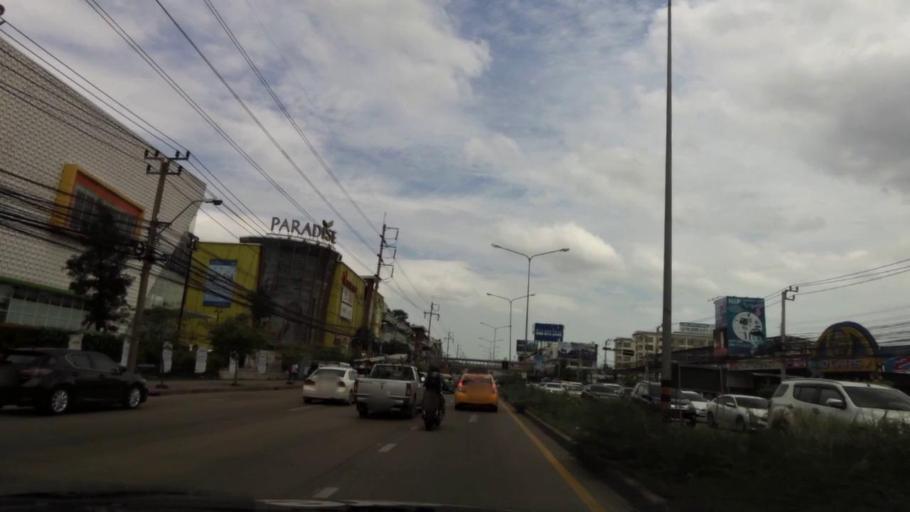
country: TH
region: Bangkok
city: Bang Na
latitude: 13.6899
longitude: 100.6471
